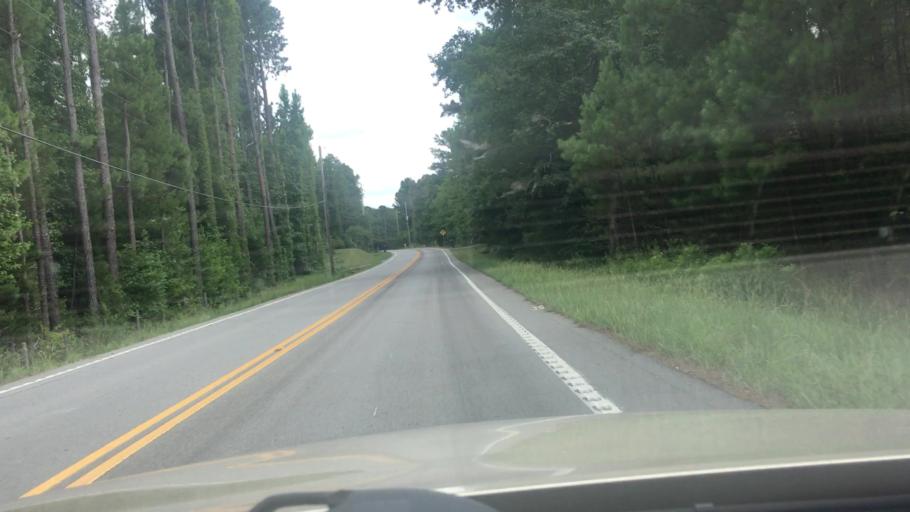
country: US
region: South Carolina
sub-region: Lexington County
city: Irmo
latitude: 34.1441
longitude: -81.1922
